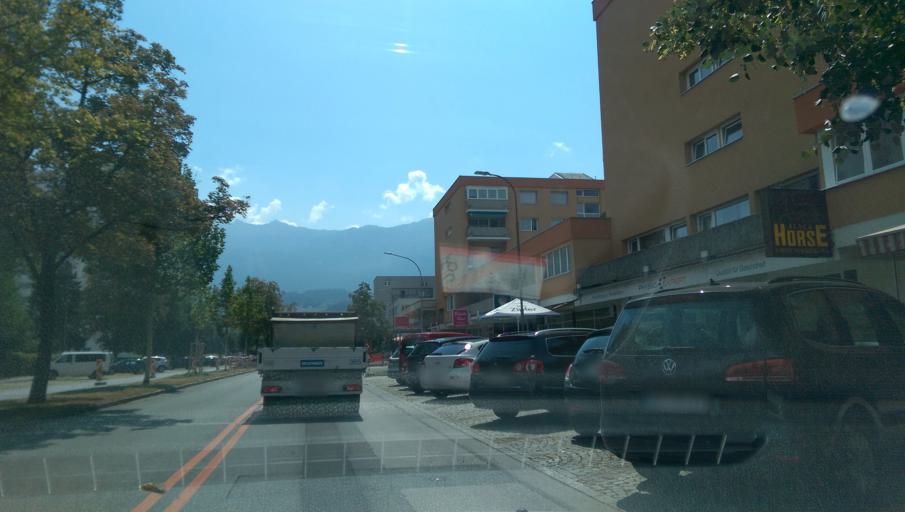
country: AT
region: Tyrol
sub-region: Innsbruck Stadt
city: Innsbruck
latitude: 47.2689
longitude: 11.4203
